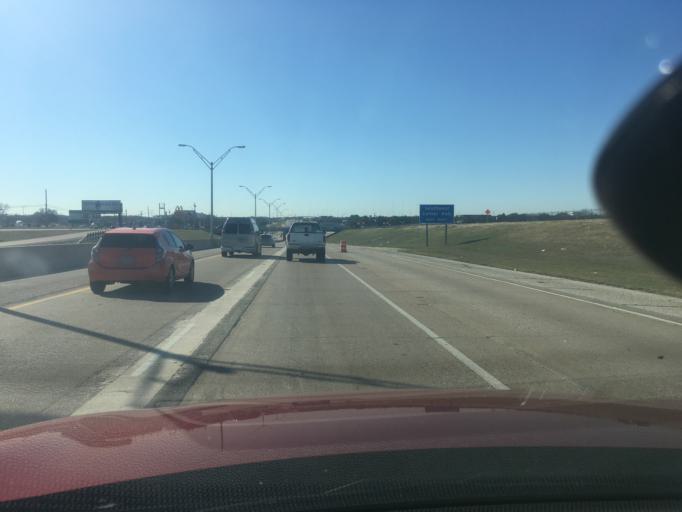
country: US
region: Texas
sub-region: Dallas County
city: Duncanville
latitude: 32.6736
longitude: -96.8600
